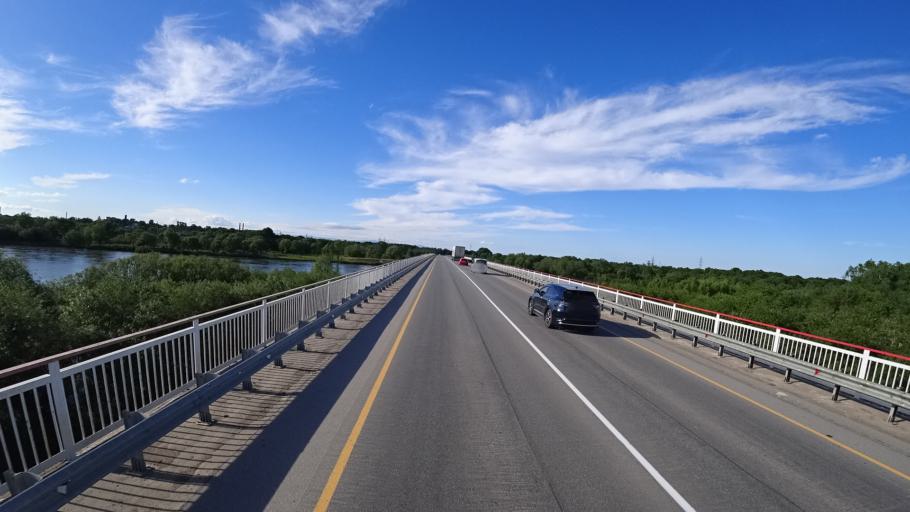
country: RU
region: Khabarovsk Krai
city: Khor
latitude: 47.8638
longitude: 134.9636
